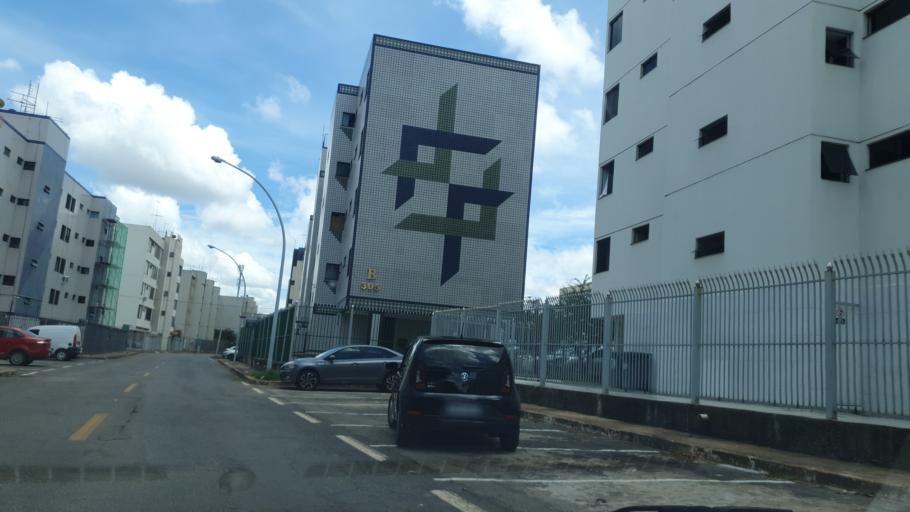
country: BR
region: Federal District
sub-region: Brasilia
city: Brasilia
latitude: -15.7982
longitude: -47.9432
